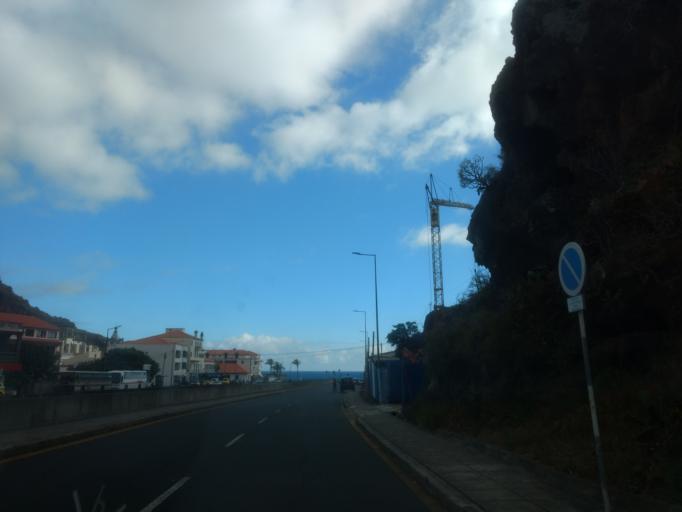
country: PT
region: Madeira
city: Ribeira Brava
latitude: 32.6732
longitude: -17.0647
